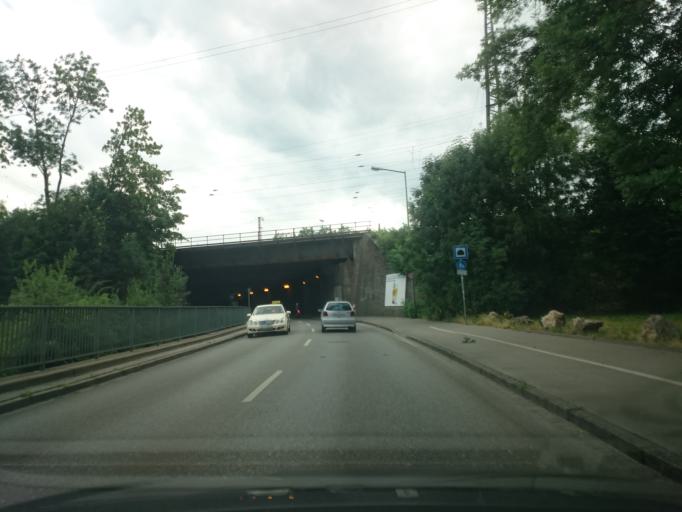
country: DE
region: Bavaria
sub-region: Swabia
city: Augsburg
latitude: 48.3729
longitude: 10.8803
